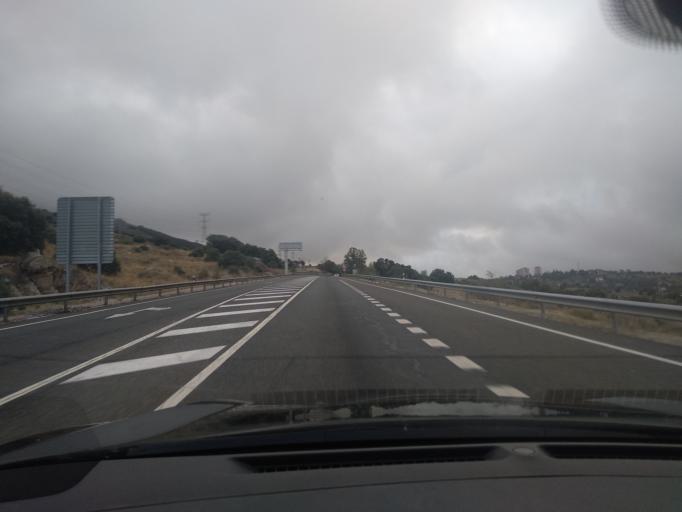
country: ES
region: Castille and Leon
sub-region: Provincia de Segovia
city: Otero de Herreros
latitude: 40.7893
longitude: -4.2143
